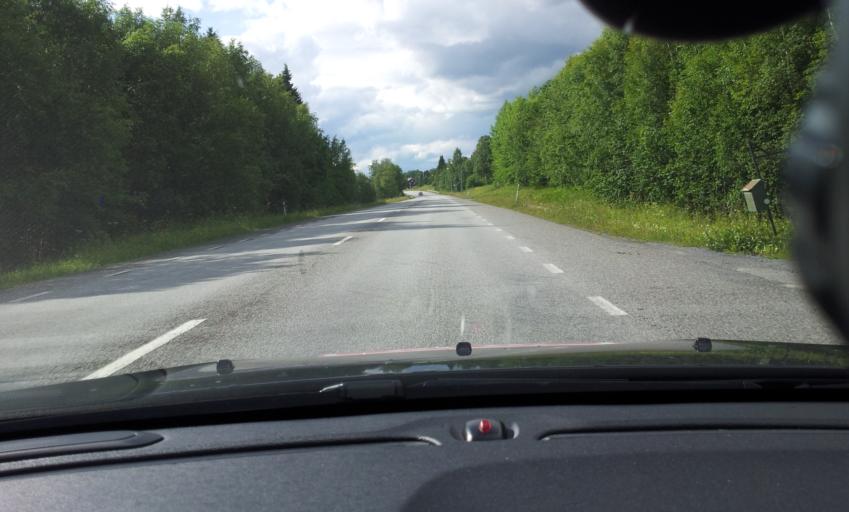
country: SE
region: Jaemtland
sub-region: Are Kommun
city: Jarpen
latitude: 63.3128
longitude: 13.6002
